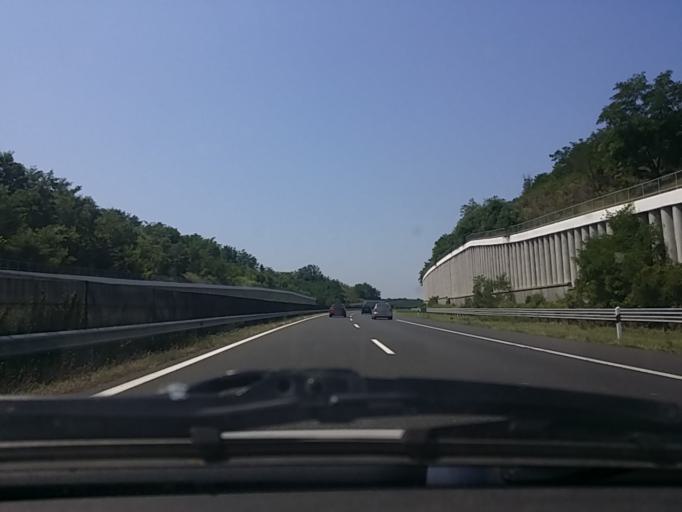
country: HU
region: Somogy
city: Balatonszarszo
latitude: 46.7924
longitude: 17.7963
